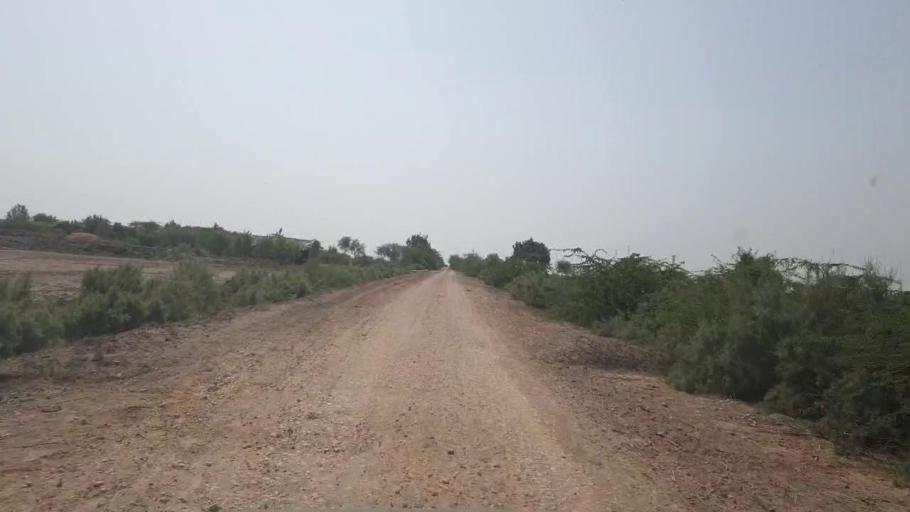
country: PK
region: Sindh
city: Jati
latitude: 24.3808
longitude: 68.6020
